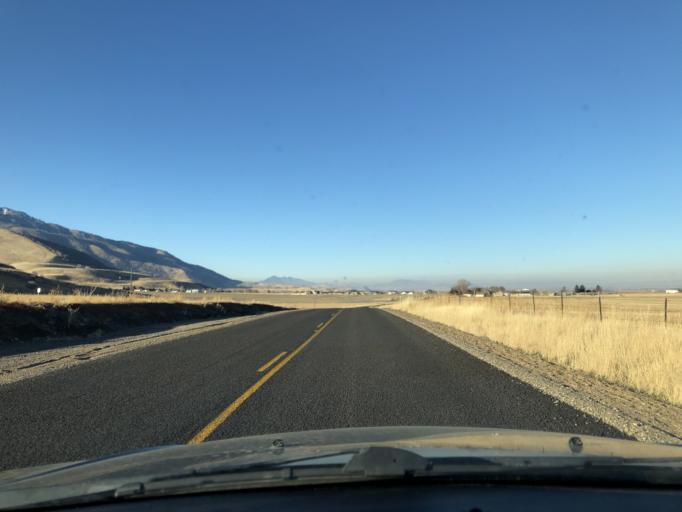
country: US
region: Utah
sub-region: Cache County
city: Wellsville
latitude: 41.5967
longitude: -111.9281
